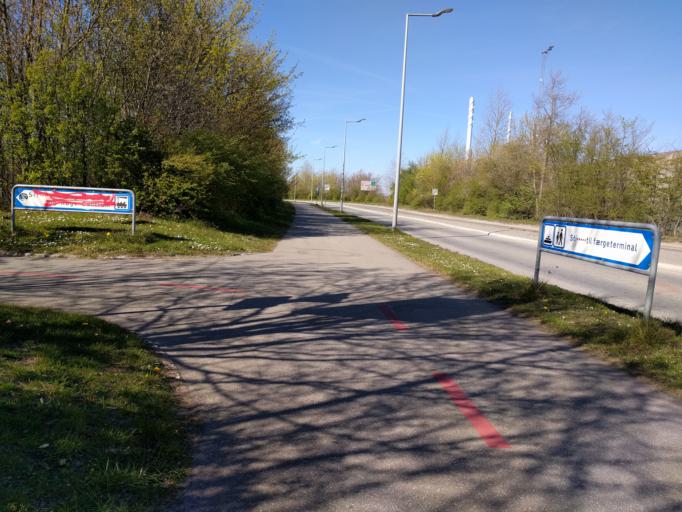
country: DK
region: Zealand
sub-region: Koge Kommune
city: Koge
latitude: 55.4571
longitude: 12.1893
